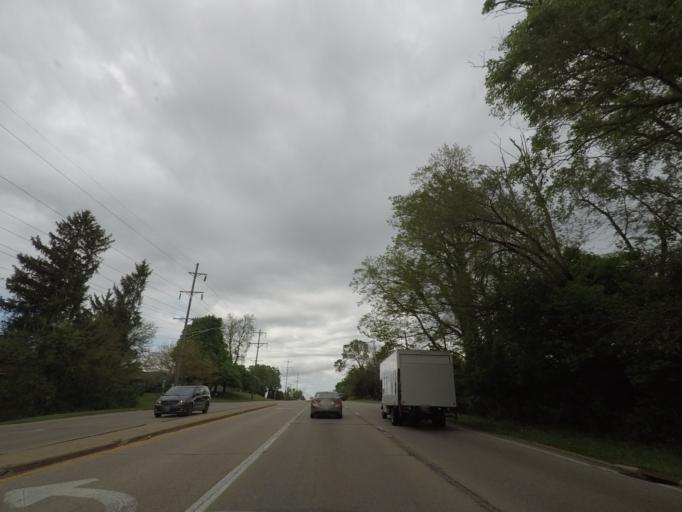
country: US
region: Illinois
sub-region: Winnebago County
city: Loves Park
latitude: 42.3000
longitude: -89.0290
